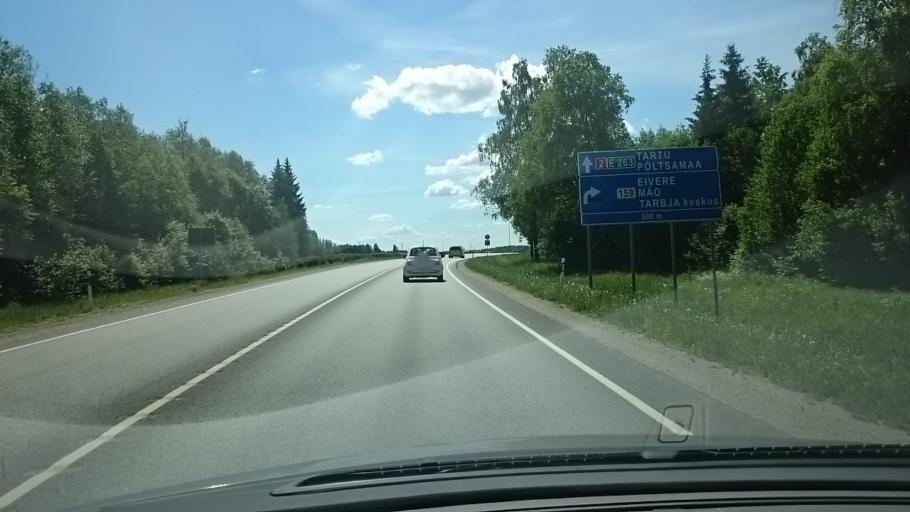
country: EE
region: Jaervamaa
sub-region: Paide linn
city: Paide
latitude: 58.9432
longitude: 25.6121
